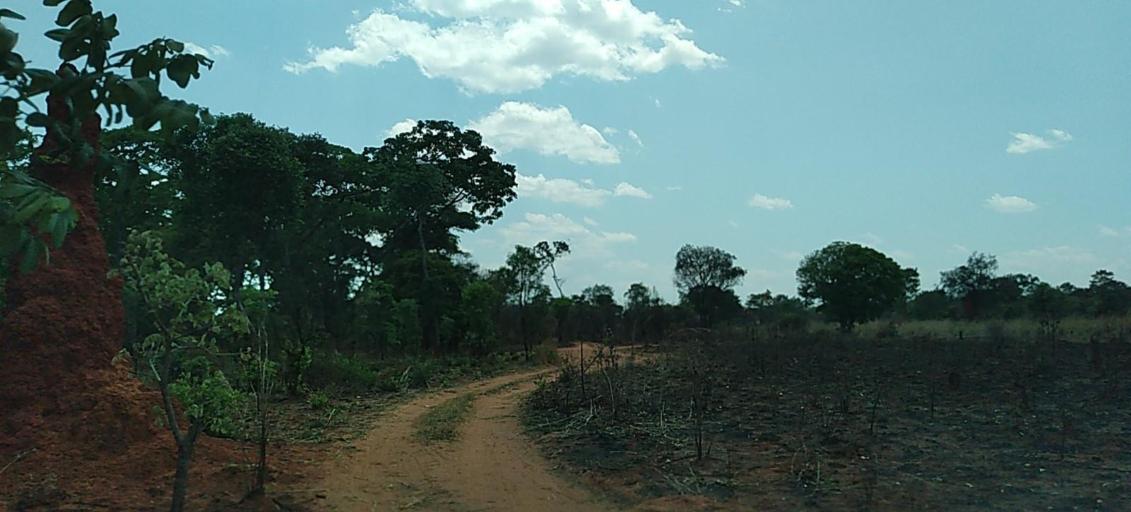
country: ZM
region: Central
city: Kapiri Mposhi
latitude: -13.6304
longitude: 28.7706
